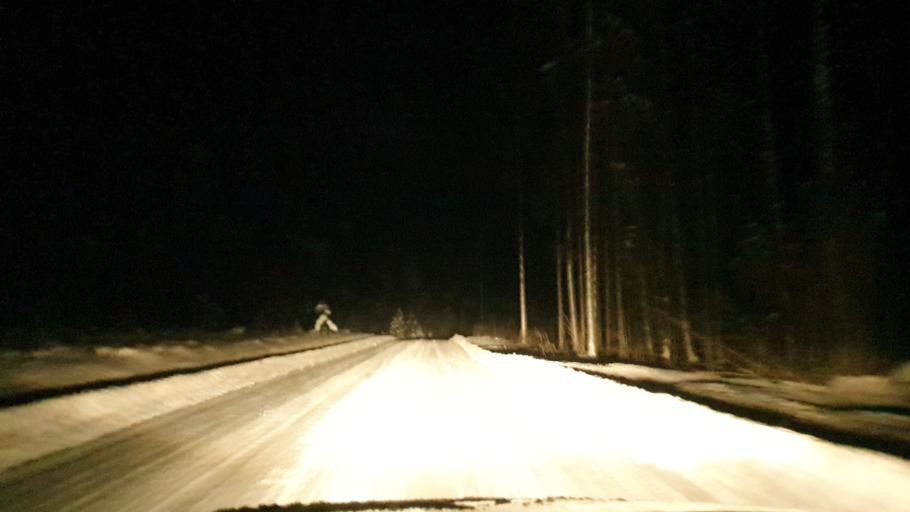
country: EE
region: Vorumaa
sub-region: Antsla vald
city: Vana-Antsla
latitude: 57.9461
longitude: 26.6089
